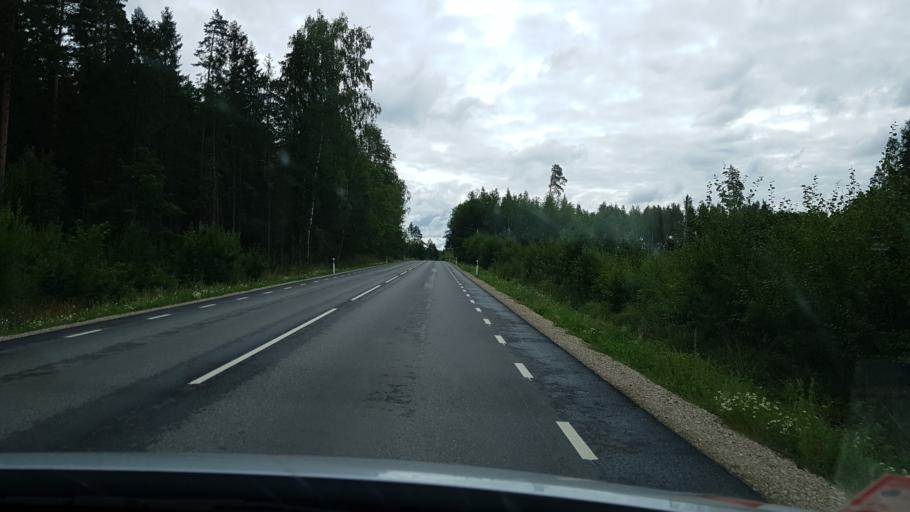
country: EE
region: Polvamaa
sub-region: Polva linn
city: Polva
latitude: 58.0099
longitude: 27.1880
